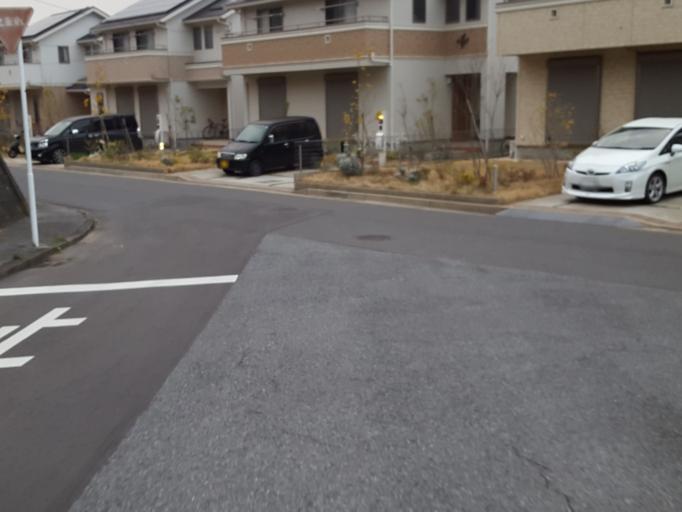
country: JP
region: Chiba
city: Ichihara
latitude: 35.4537
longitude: 140.0539
